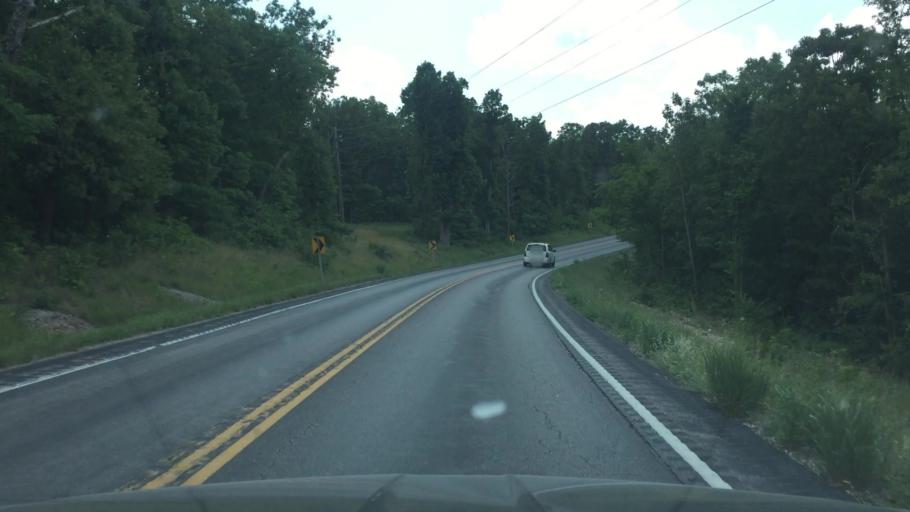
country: US
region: Missouri
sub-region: Miller County
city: Tuscumbia
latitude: 38.0973
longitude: -92.4960
